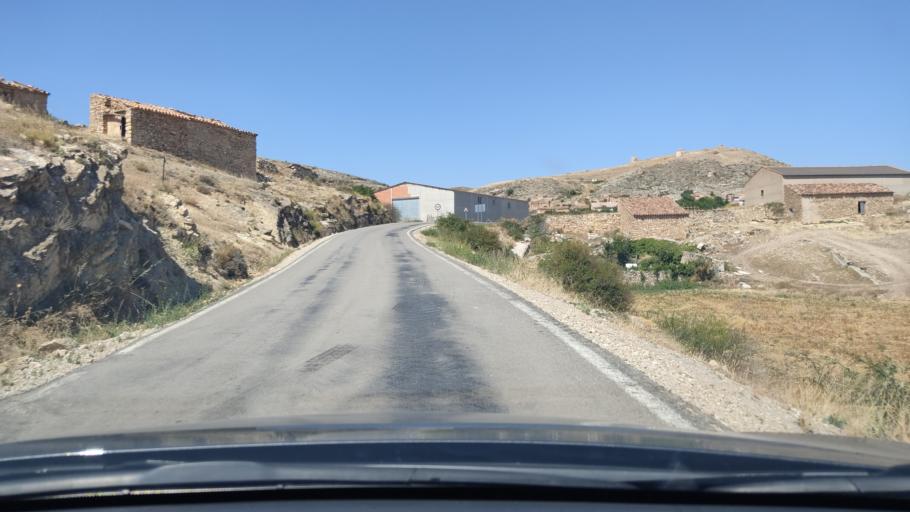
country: ES
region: Aragon
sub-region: Provincia de Teruel
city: Monforte de Moyuela
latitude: 41.0513
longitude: -1.0111
